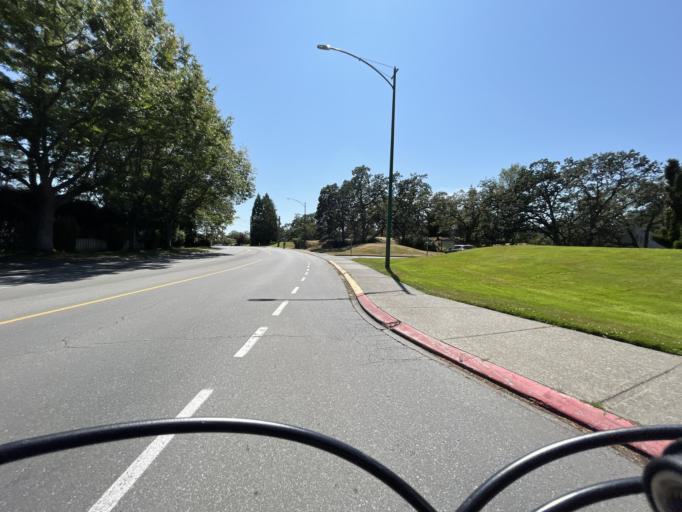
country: CA
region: British Columbia
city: Oak Bay
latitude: 48.4474
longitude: -123.3214
